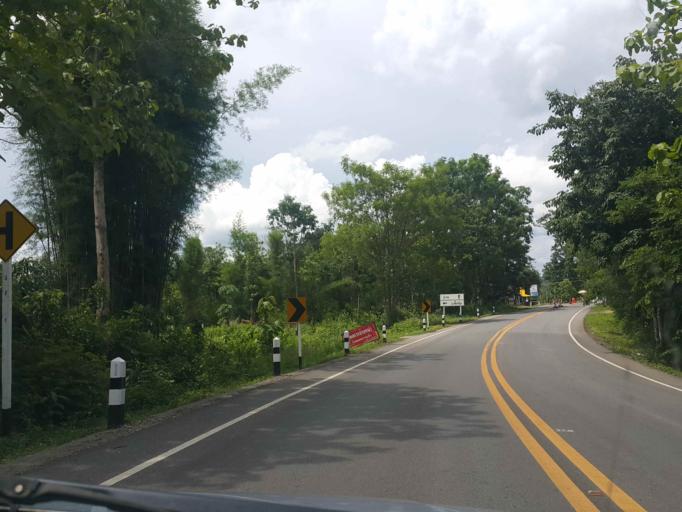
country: TH
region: Nan
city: Ban Luang
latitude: 18.8576
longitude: 100.4541
